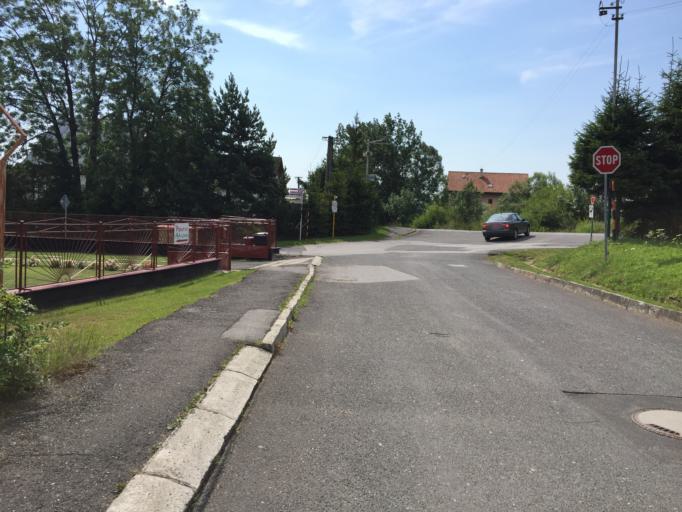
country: SK
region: Presovsky
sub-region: Okres Poprad
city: Nova Lesna
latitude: 49.1229
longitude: 20.2635
